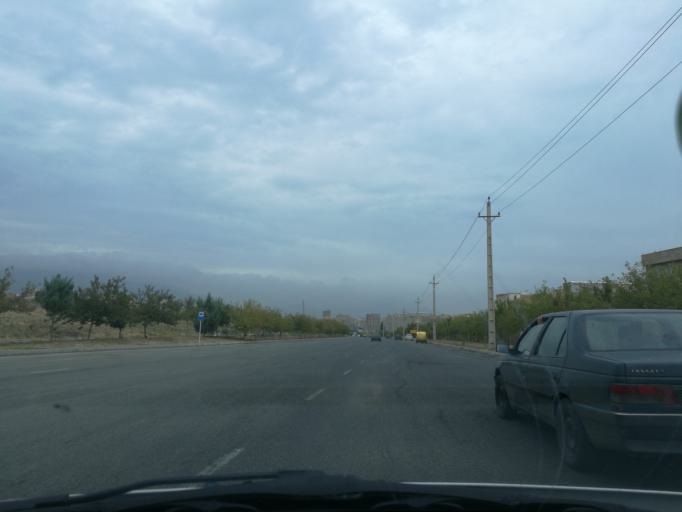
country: IR
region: Alborz
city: Karaj
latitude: 35.8645
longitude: 50.9285
